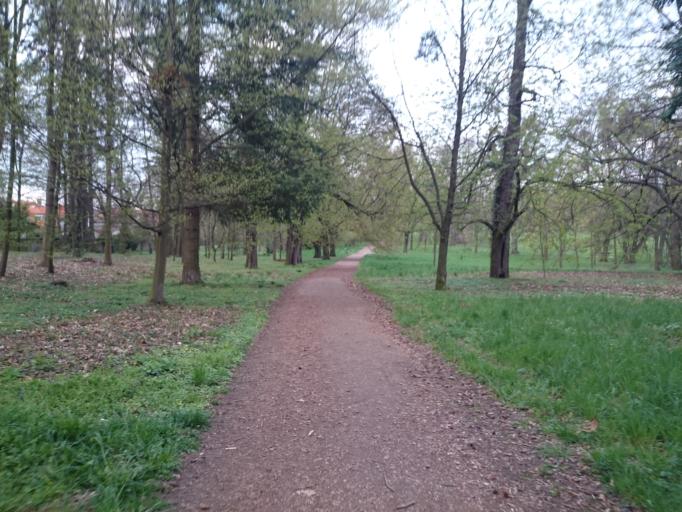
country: CZ
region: Pardubicky
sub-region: Okres Chrudim
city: Hermanuv Mestec
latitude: 49.9431
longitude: 15.6651
